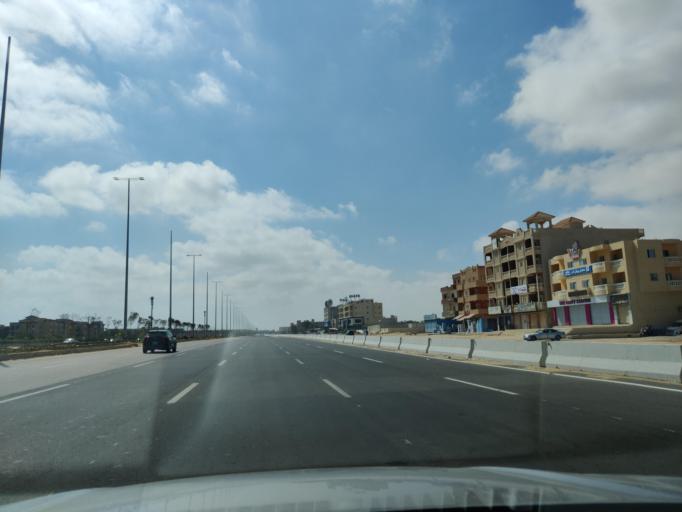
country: EG
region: Muhafazat Matruh
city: Al `Alamayn
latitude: 30.9644
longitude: 28.7508
